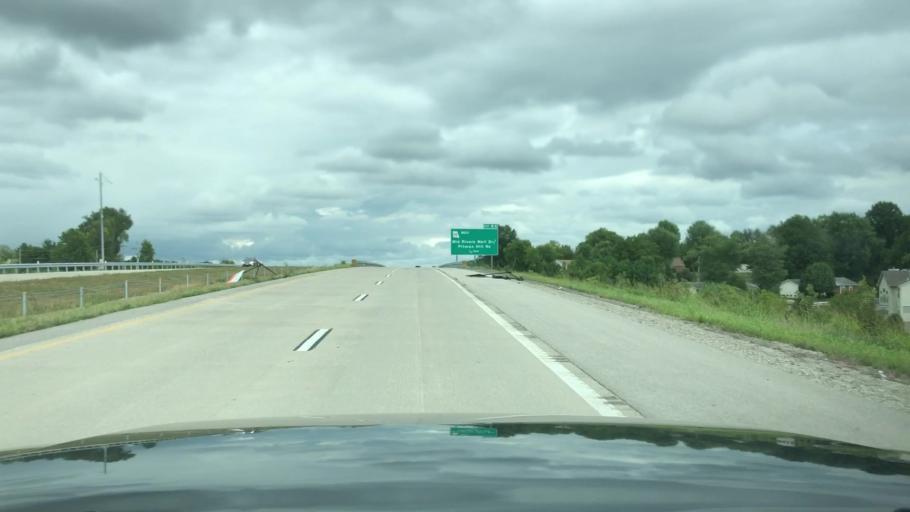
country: US
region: Missouri
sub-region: Saint Charles County
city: Cottleville
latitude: 38.7330
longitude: -90.6526
